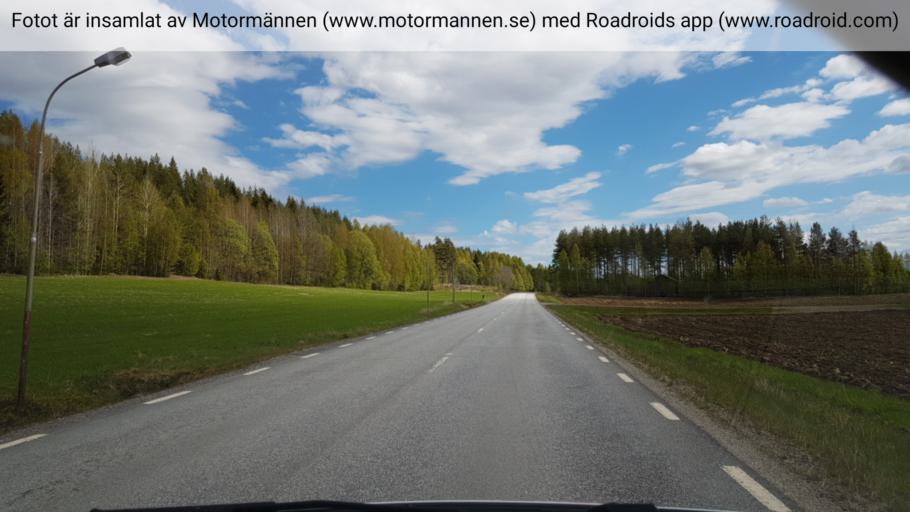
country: SE
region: Vaesterbotten
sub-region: Bjurholms Kommun
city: Bjurholm
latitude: 64.2406
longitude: 19.3333
